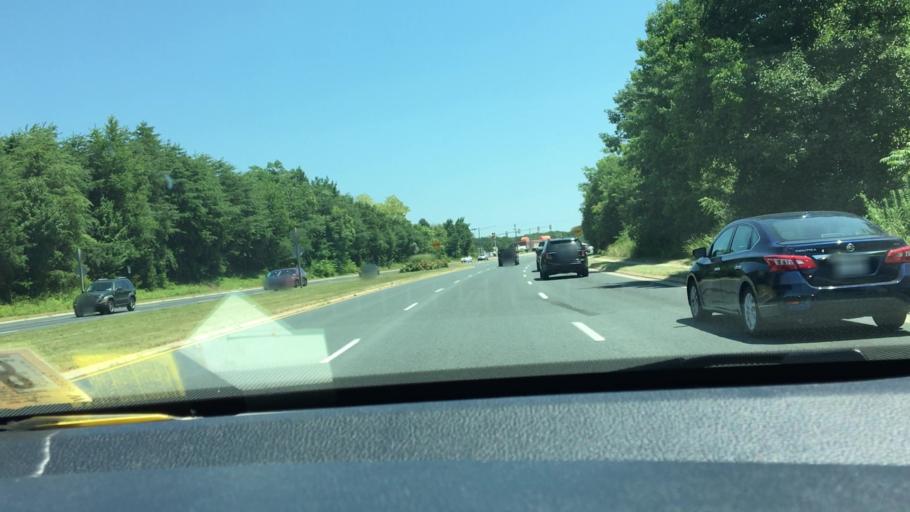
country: US
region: Virginia
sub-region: Prince William County
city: Potomac Mills
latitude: 38.6496
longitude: -77.3051
